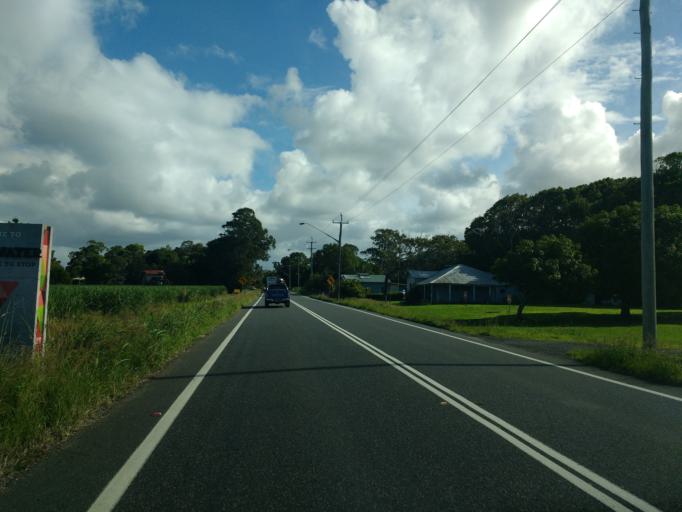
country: AU
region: New South Wales
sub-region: Richmond Valley
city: Evans Head
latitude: -29.0009
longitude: 153.4386
